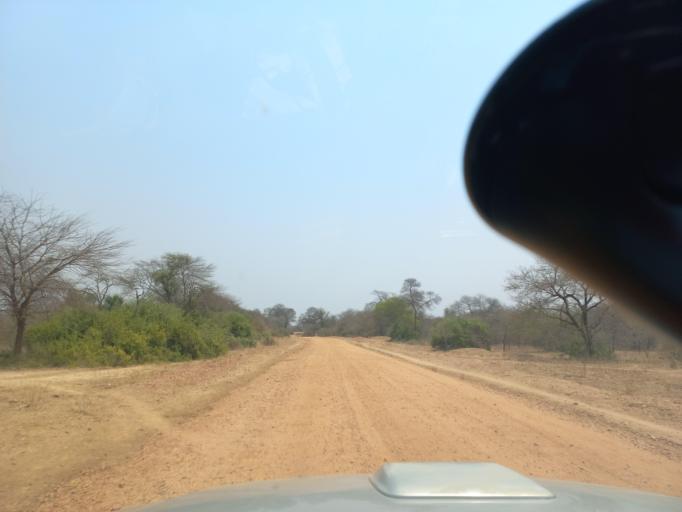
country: ZW
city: Chirundu
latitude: -15.9446
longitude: 28.8184
